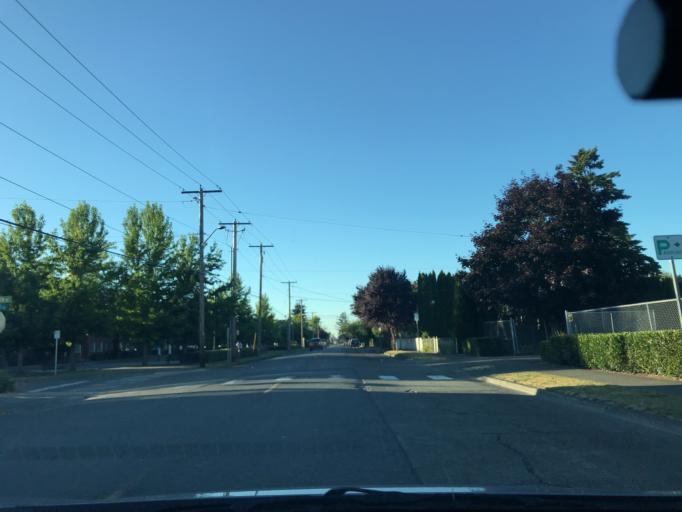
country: US
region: Washington
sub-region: Pierce County
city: Sumner
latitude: 47.2039
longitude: -122.2373
